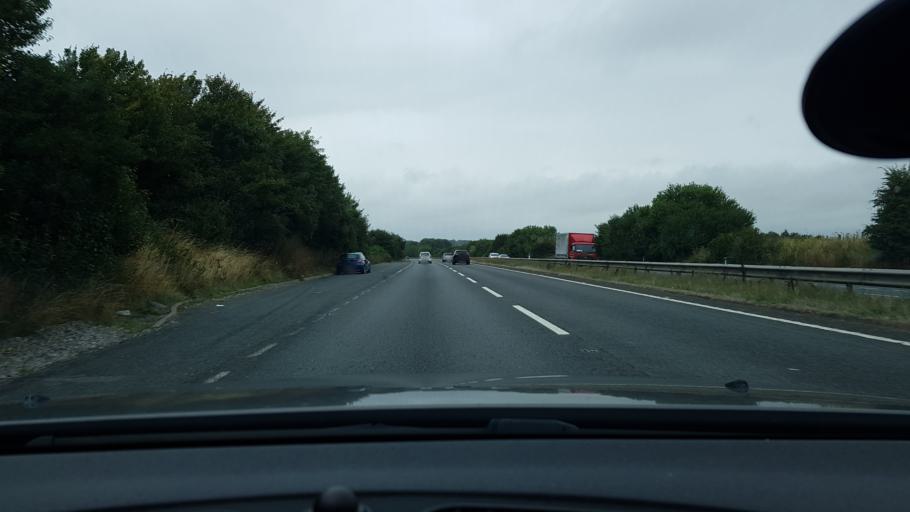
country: GB
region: England
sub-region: Hampshire
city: Kings Worthy
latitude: 51.1324
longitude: -1.3452
